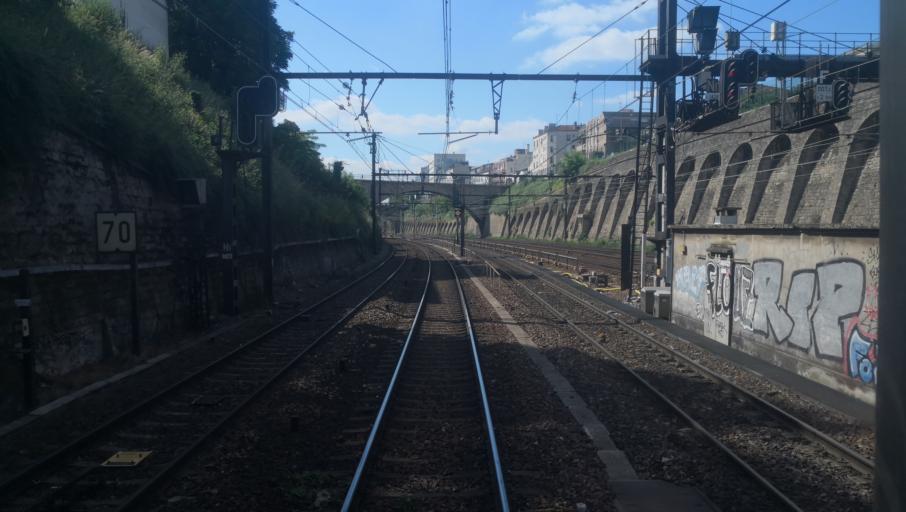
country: FR
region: Ile-de-France
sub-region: Departement du Val-de-Marne
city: Charenton-le-Pont
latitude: 48.8226
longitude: 2.4092
